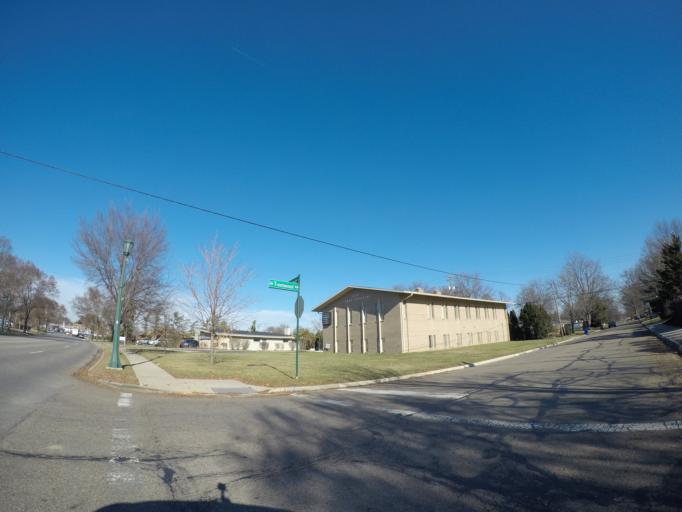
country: US
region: Ohio
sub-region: Franklin County
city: Upper Arlington
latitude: 40.0232
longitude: -83.0570
